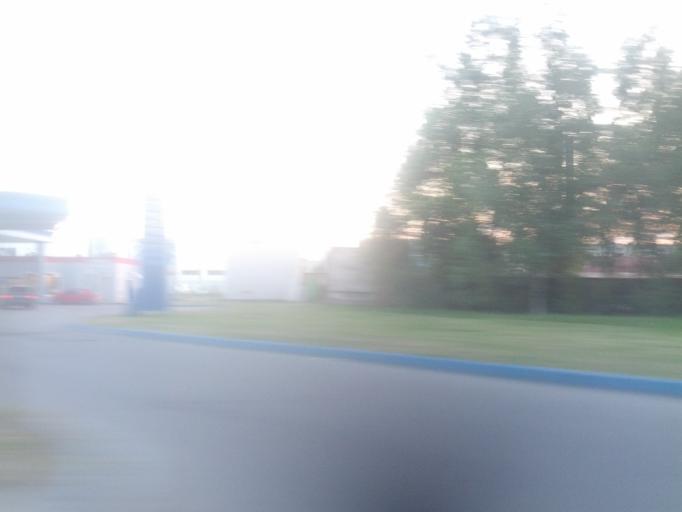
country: RU
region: St.-Petersburg
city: Staraya Derevnya
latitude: 59.9926
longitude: 30.2556
